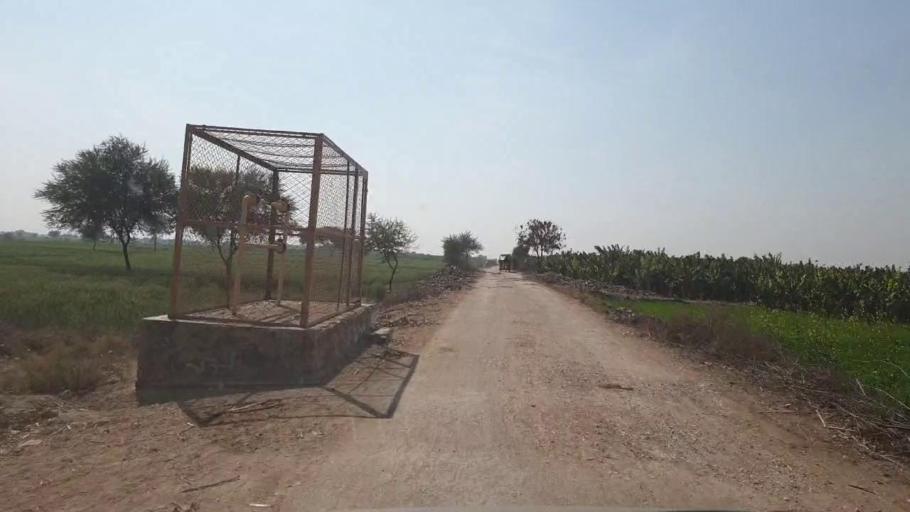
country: PK
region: Sindh
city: Chambar
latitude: 25.3493
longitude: 68.8230
